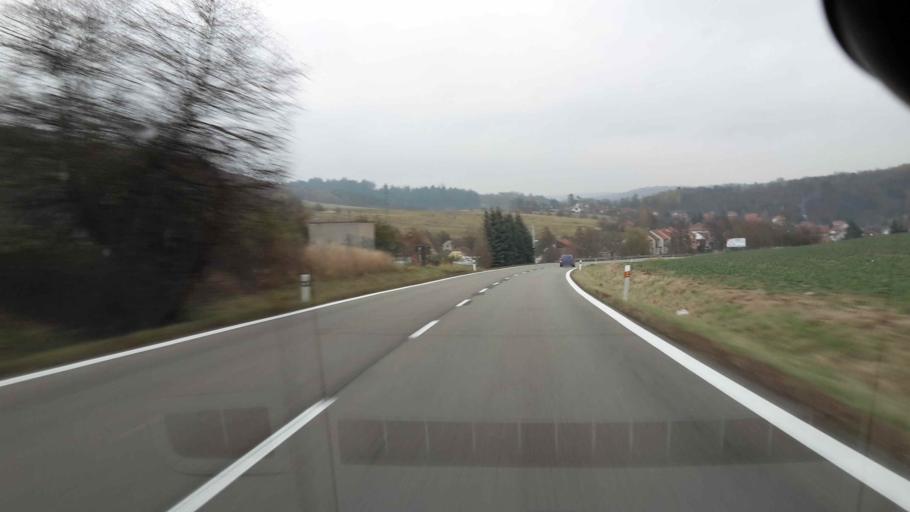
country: CZ
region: South Moravian
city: Lipuvka
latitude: 49.3316
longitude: 16.5892
